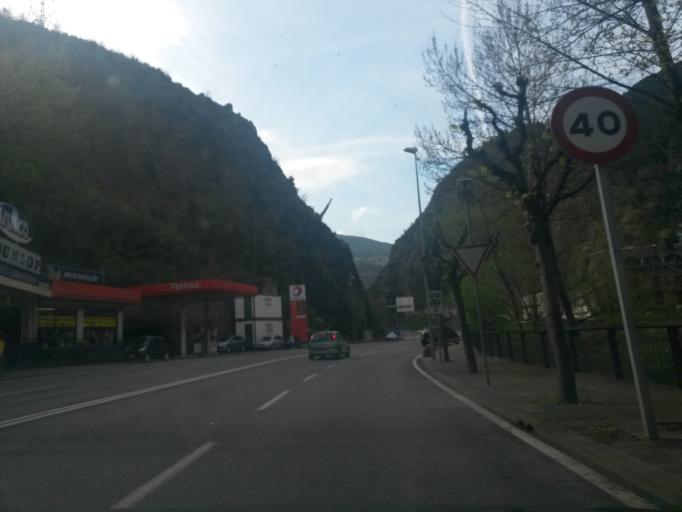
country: AD
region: Sant Julia de Loria
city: Sant Julia de Loria
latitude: 42.4773
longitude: 1.4906
